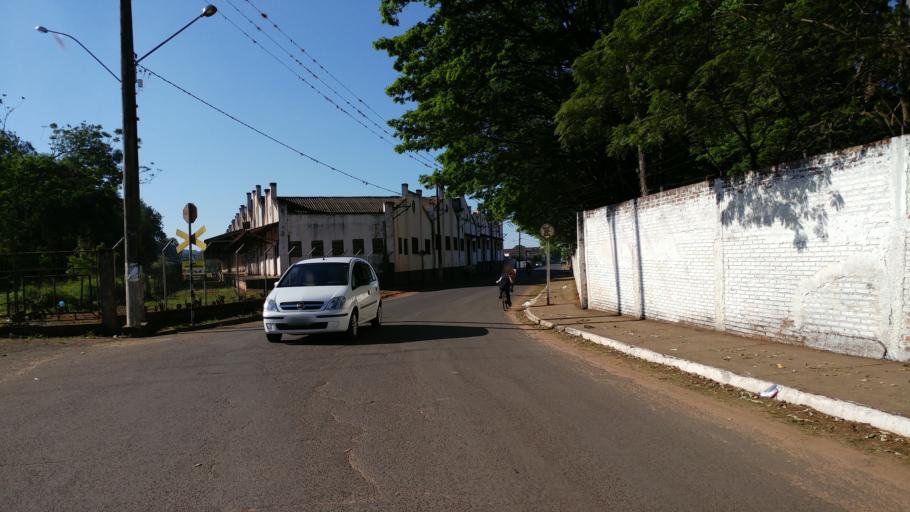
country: BR
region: Sao Paulo
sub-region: Paraguacu Paulista
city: Paraguacu Paulista
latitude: -22.4218
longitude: -50.5729
